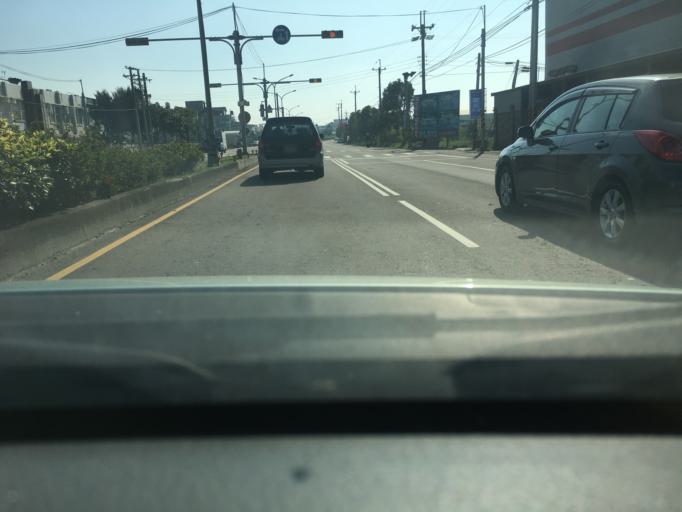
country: TW
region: Taiwan
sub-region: Hsinchu
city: Hsinchu
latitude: 24.8146
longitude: 120.9227
